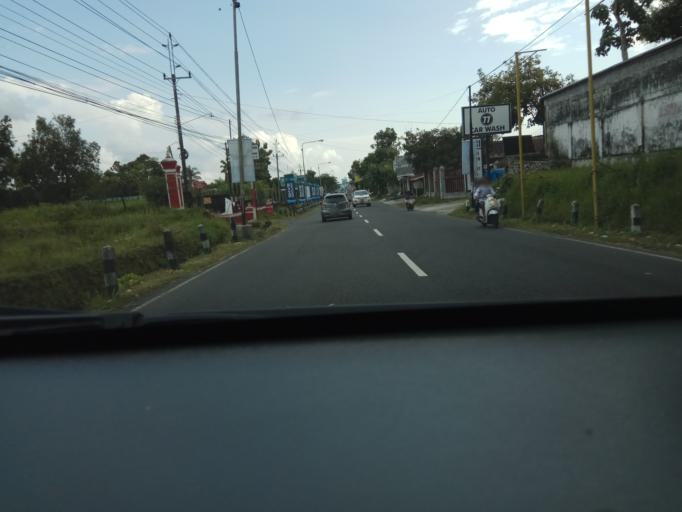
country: ID
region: Daerah Istimewa Yogyakarta
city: Melati
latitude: -7.7156
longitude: 110.4062
